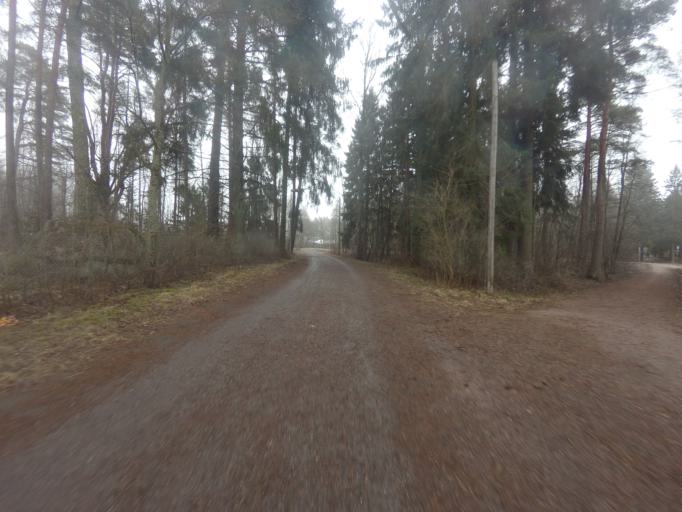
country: FI
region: Uusimaa
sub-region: Helsinki
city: Koukkuniemi
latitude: 60.1477
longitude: 24.7105
